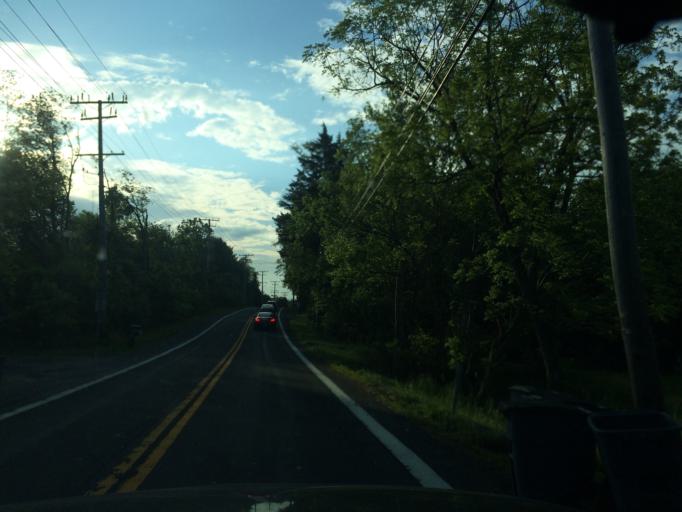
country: US
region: Maryland
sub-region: Carroll County
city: Sykesville
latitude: 39.3189
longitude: -77.0153
